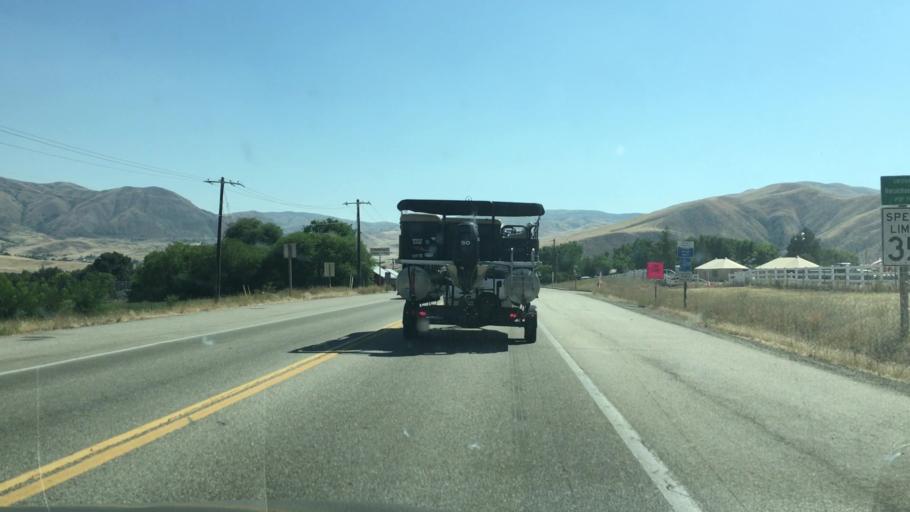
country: US
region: Idaho
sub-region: Ada County
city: Eagle
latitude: 43.9207
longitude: -116.1955
